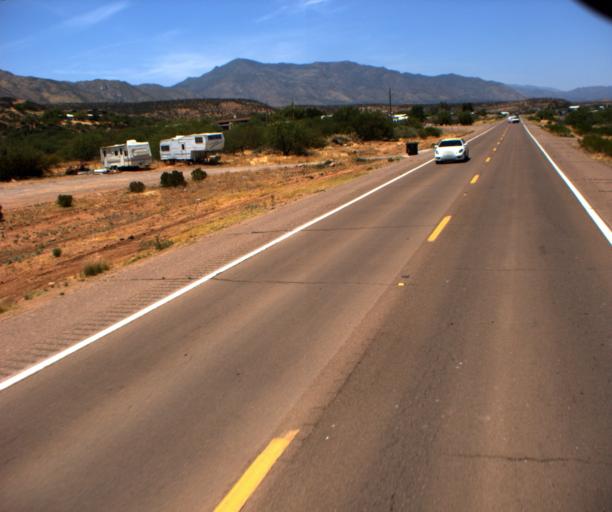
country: US
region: Arizona
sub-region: Gila County
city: Tonto Basin
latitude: 33.8398
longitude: -111.3037
